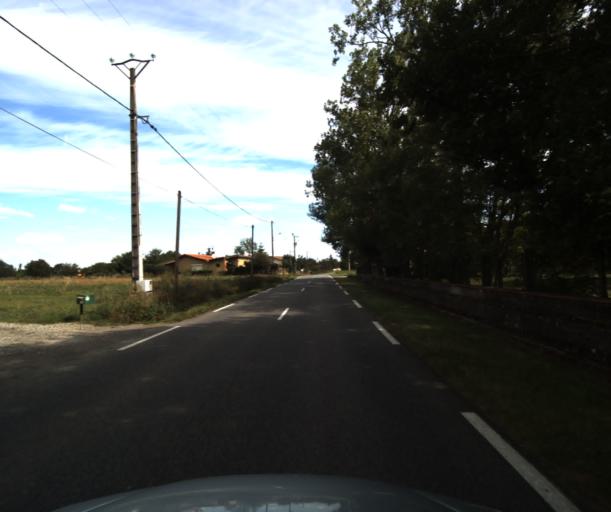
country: FR
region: Midi-Pyrenees
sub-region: Departement de la Haute-Garonne
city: Seysses
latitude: 43.4776
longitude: 1.3041
